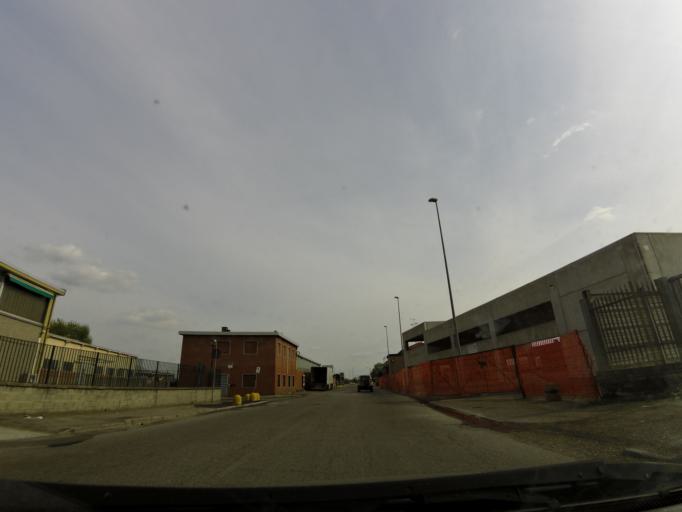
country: IT
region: Lombardy
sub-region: Citta metropolitana di Milano
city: Civesio
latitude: 45.3938
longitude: 9.2563
